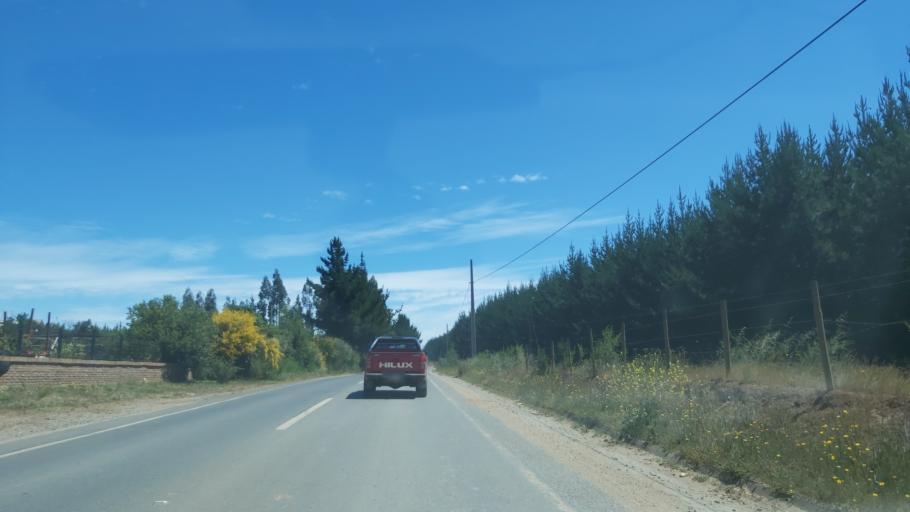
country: CL
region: Maule
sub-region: Provincia de Talca
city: Constitucion
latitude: -35.3926
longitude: -72.4262
